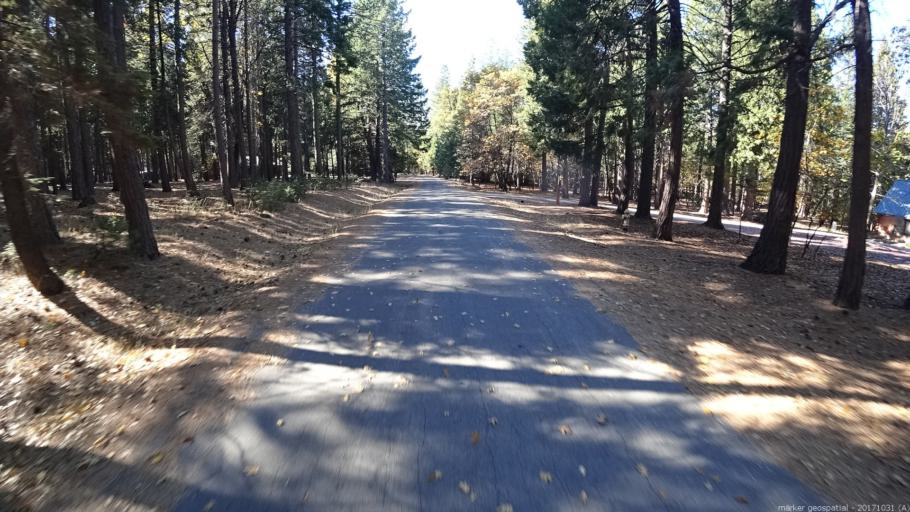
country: US
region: California
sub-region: Shasta County
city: Shingletown
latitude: 40.4901
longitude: -121.8876
